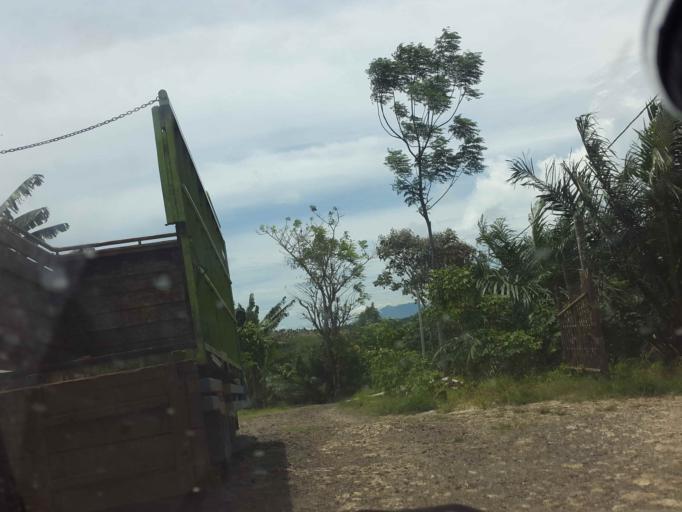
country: ID
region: Lampung
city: Sidorejo
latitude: -5.5799
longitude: 105.4588
